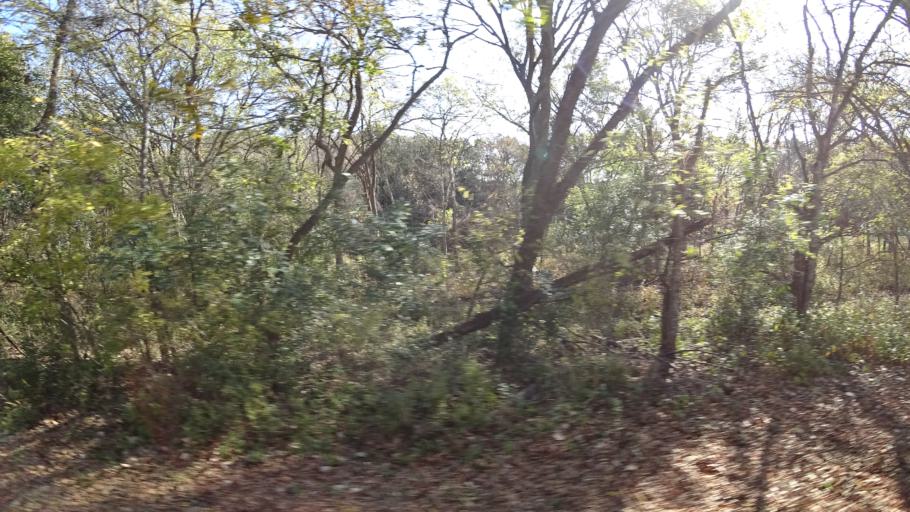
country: US
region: Texas
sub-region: Williamson County
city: Jollyville
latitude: 30.3932
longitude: -97.7778
